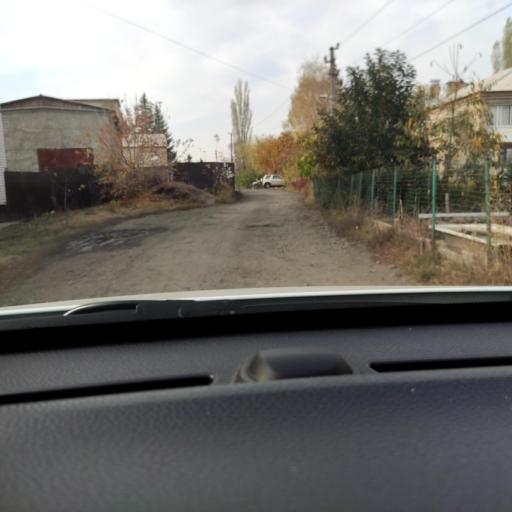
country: RU
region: Voronezj
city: Novaya Usman'
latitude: 51.6106
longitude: 39.3819
